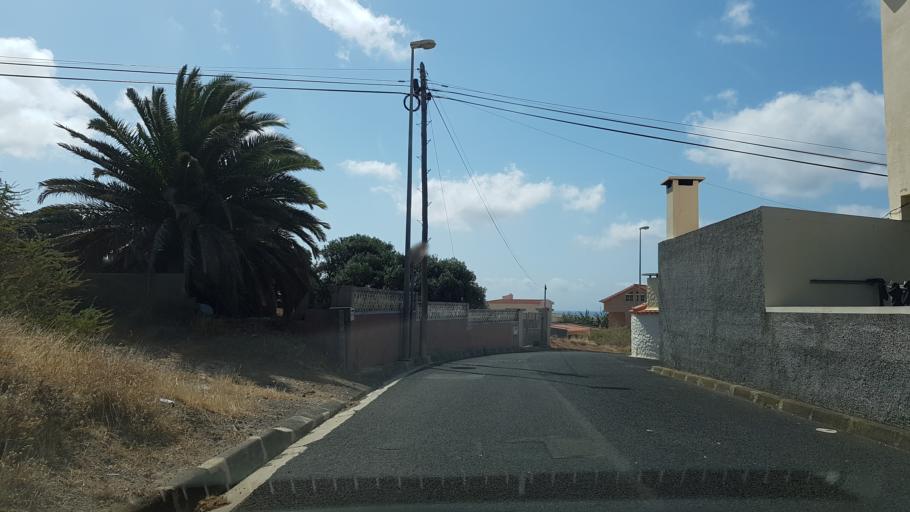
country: PT
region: Madeira
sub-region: Porto Santo
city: Vila de Porto Santo
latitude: 33.0660
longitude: -16.3287
